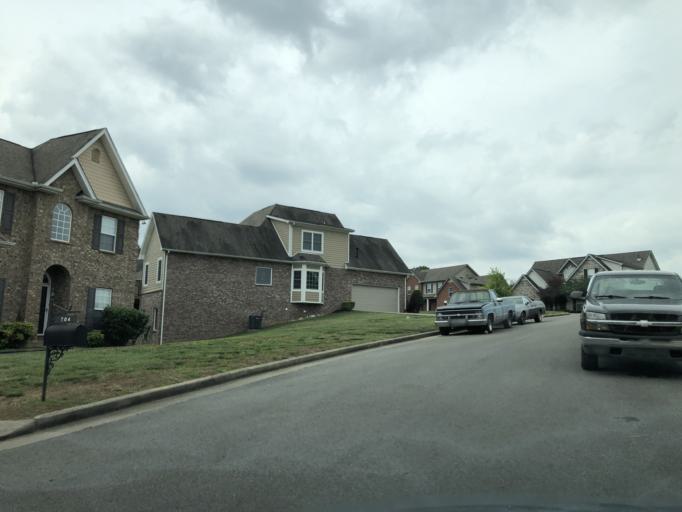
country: US
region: Tennessee
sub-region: Davidson County
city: Goodlettsville
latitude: 36.2820
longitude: -86.7441
